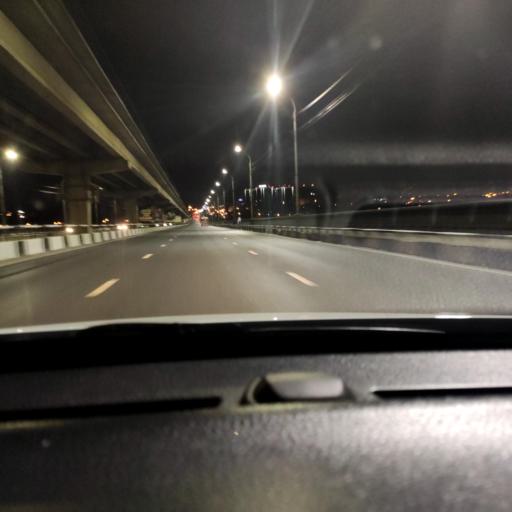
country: RU
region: Voronezj
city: Voronezh
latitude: 51.6908
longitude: 39.2444
